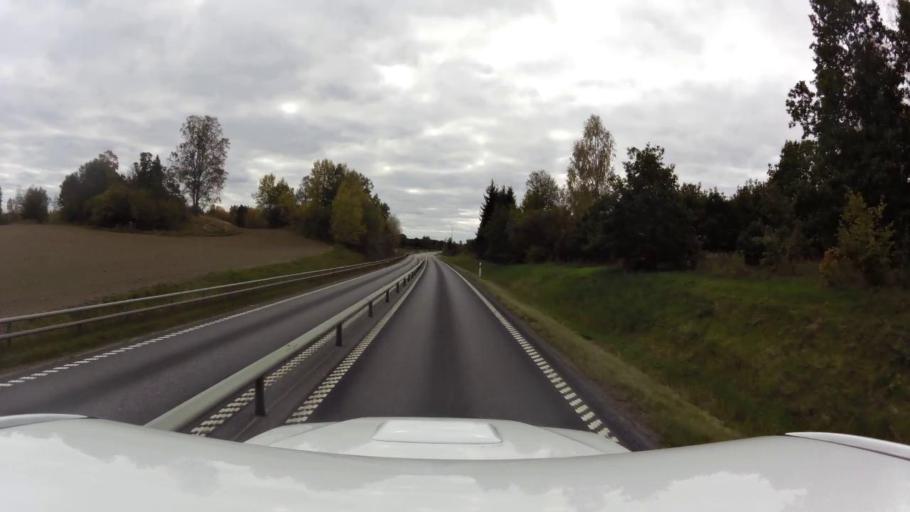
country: SE
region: OEstergoetland
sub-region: Linkopings Kommun
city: Malmslatt
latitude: 58.2894
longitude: 15.5667
